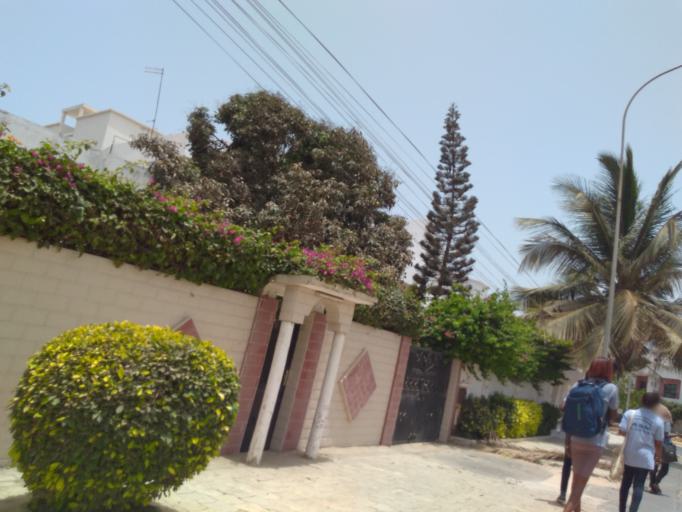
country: SN
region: Dakar
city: Grand Dakar
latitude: 14.7321
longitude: -17.4707
